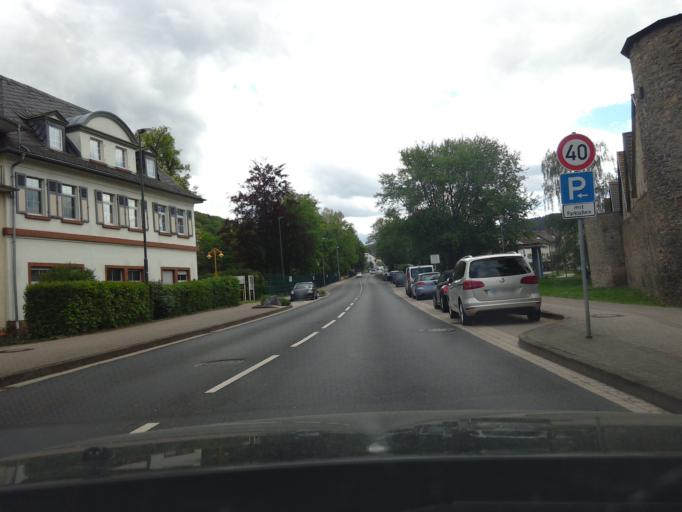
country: DE
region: Hesse
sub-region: Regierungsbezirk Darmstadt
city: Bad Orb
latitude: 50.2272
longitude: 9.3494
